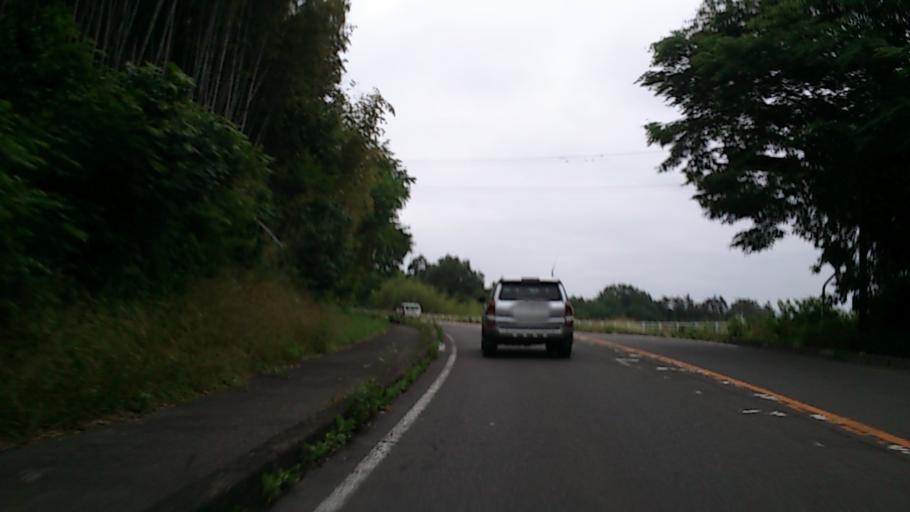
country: JP
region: Fukushima
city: Fukushima-shi
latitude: 37.6882
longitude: 140.5239
